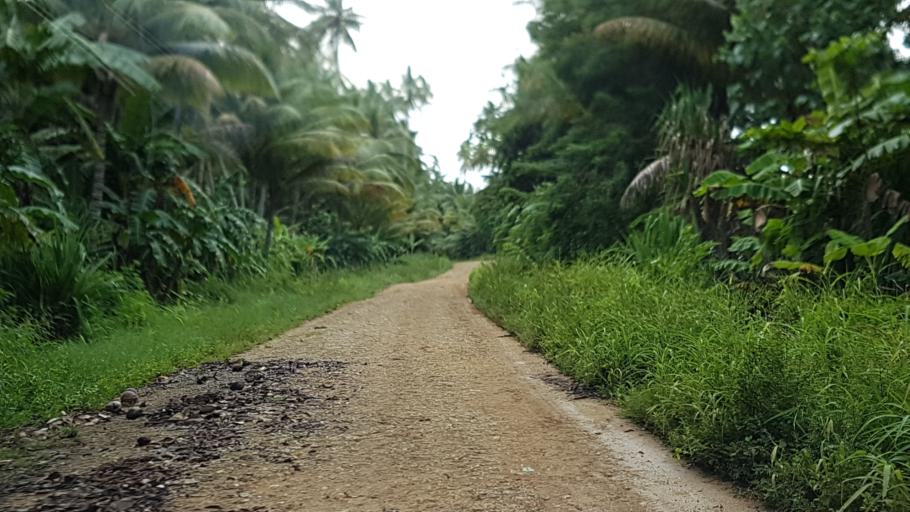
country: PG
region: Milne Bay
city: Alotau
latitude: -10.2814
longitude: 150.7783
